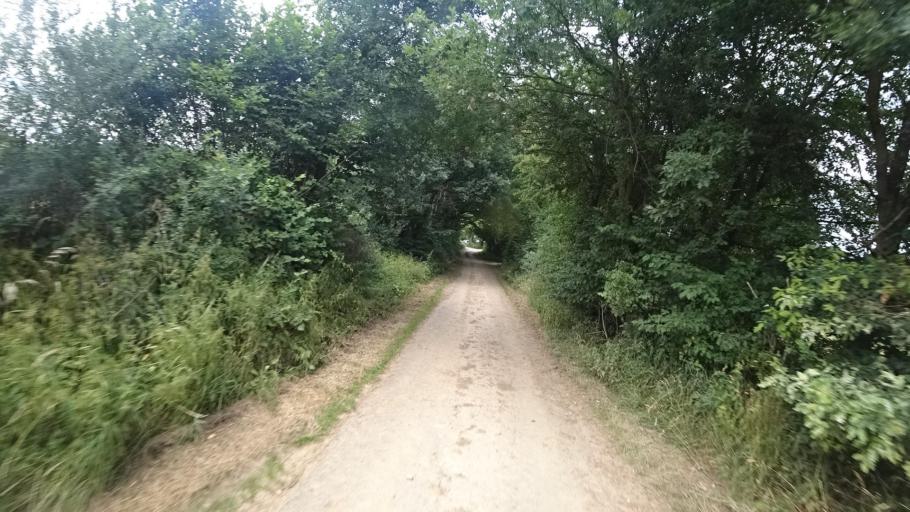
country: DE
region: Rheinland-Pfalz
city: Oberirsen
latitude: 50.7207
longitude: 7.5732
